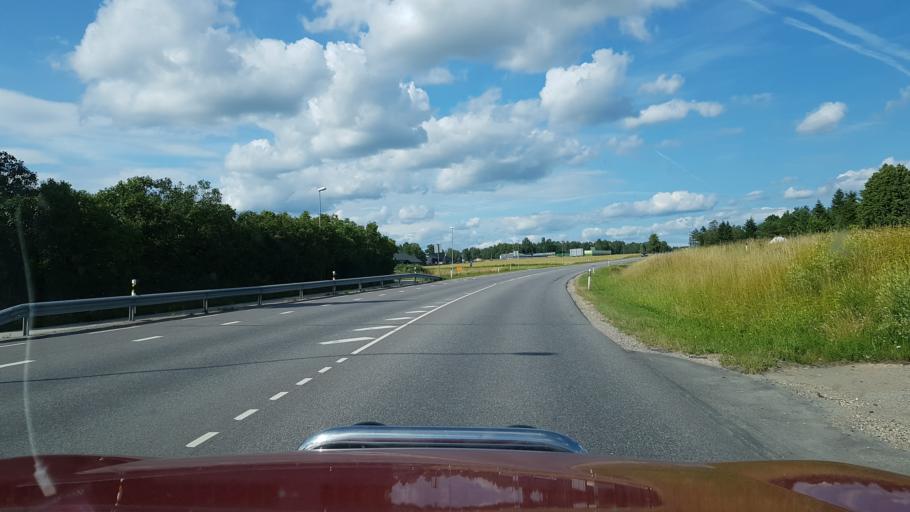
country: EE
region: Tartu
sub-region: Tartu linn
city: Tartu
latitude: 58.4603
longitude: 26.6719
